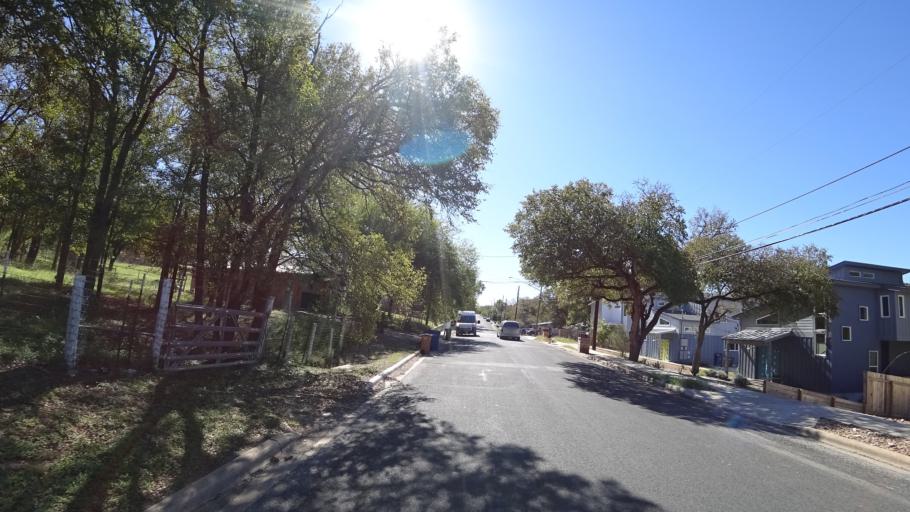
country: US
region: Texas
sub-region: Travis County
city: Austin
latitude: 30.2770
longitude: -97.6793
